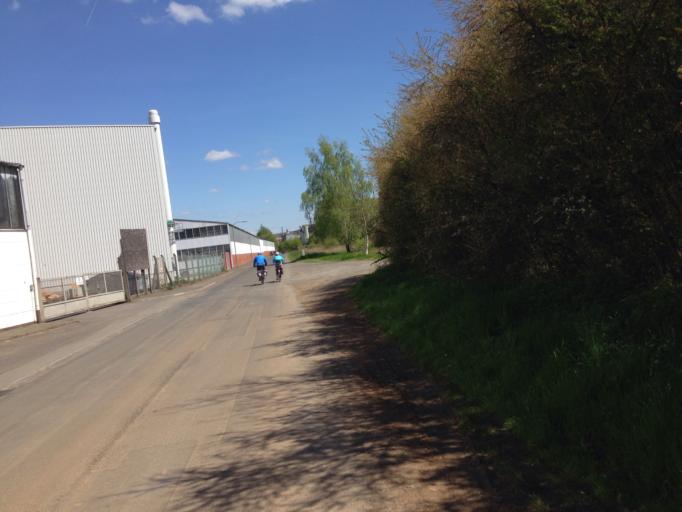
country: DE
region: Hesse
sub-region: Regierungsbezirk Giessen
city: Laubach
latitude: 50.5413
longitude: 8.9725
